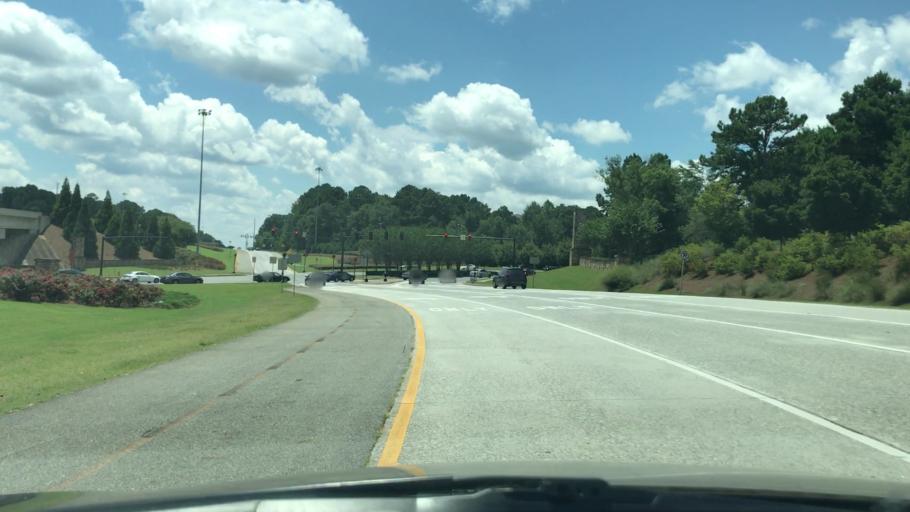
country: US
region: Georgia
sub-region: Fulton County
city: Alpharetta
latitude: 34.0891
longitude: -84.2622
